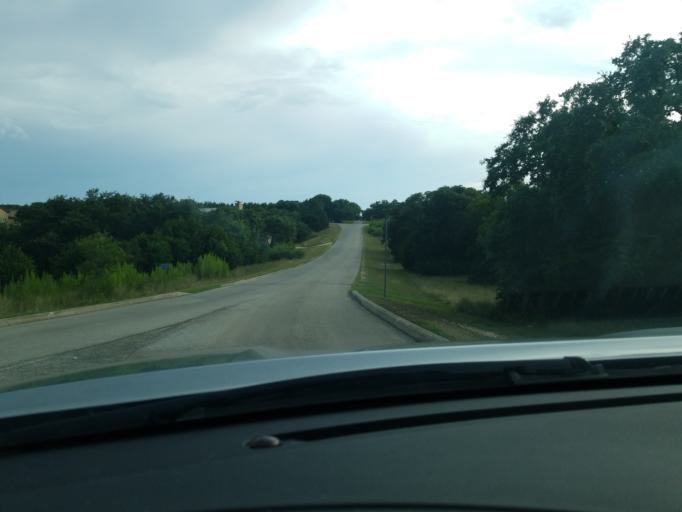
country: US
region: Texas
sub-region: Comal County
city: Bulverde
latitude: 29.8365
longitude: -98.4020
